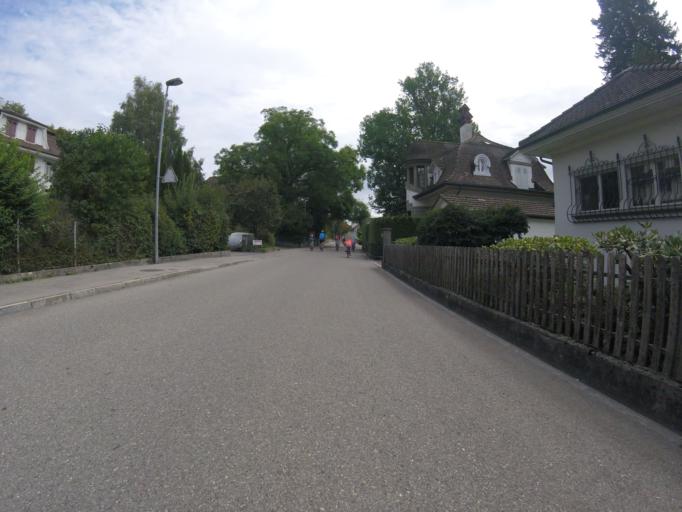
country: CH
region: Bern
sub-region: Bern-Mittelland District
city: Muri
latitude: 46.9357
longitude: 7.5082
